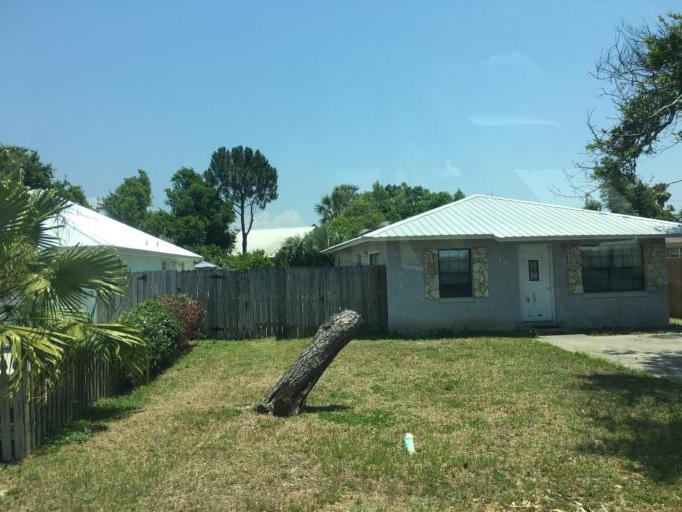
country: US
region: Florida
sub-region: Bay County
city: Panama City Beach
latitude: 30.2117
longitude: -85.8578
